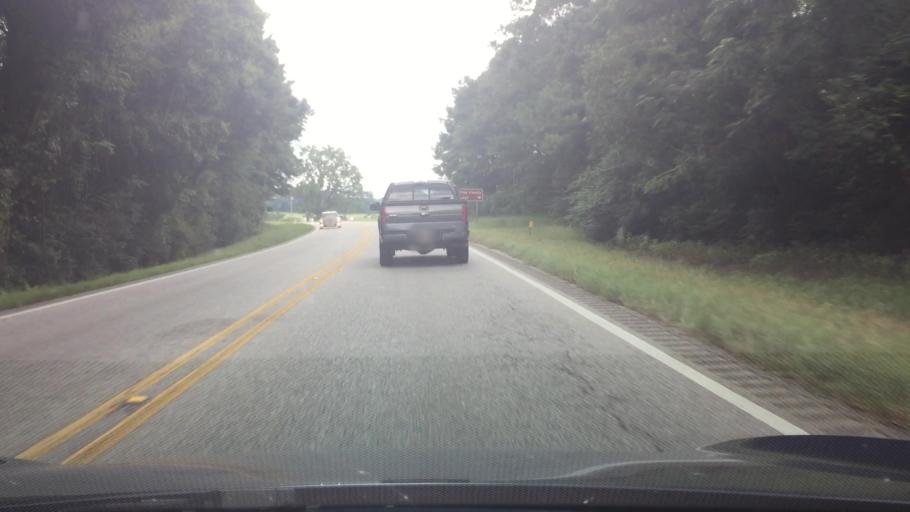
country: US
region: Alabama
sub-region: Pike County
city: Troy
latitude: 31.7478
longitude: -85.9595
